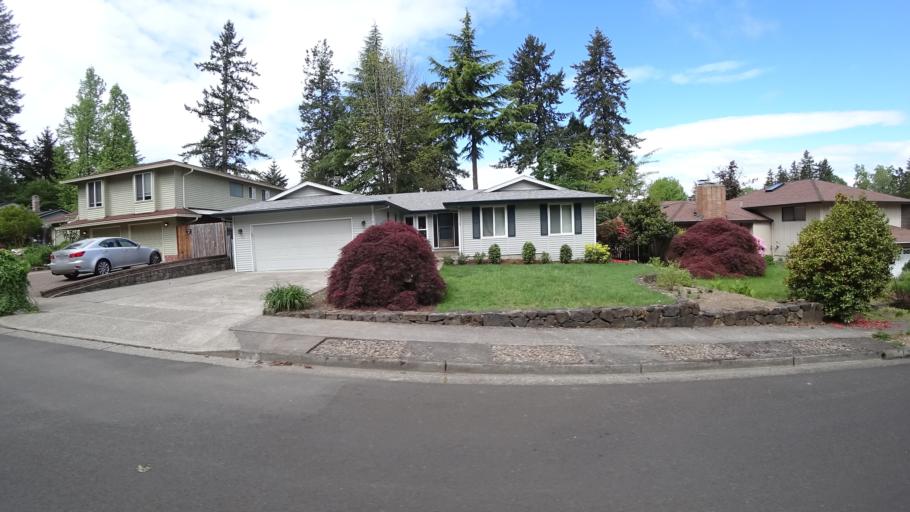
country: US
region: Oregon
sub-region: Washington County
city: Beaverton
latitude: 45.4692
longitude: -122.8138
